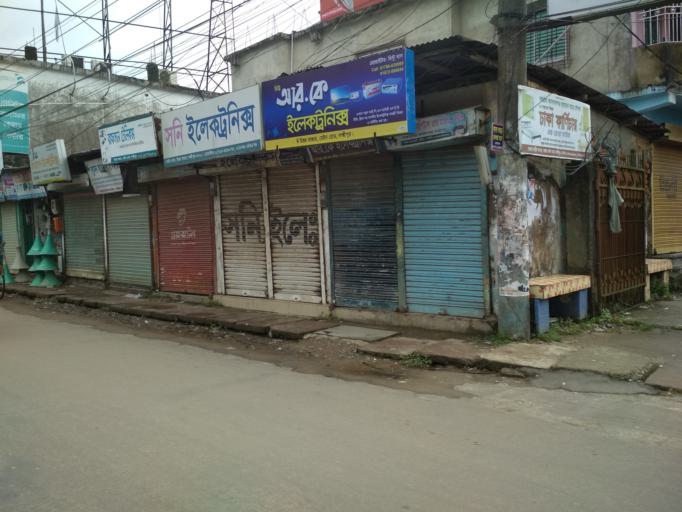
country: BD
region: Chittagong
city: Lakshmipur
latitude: 22.9431
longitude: 90.8282
